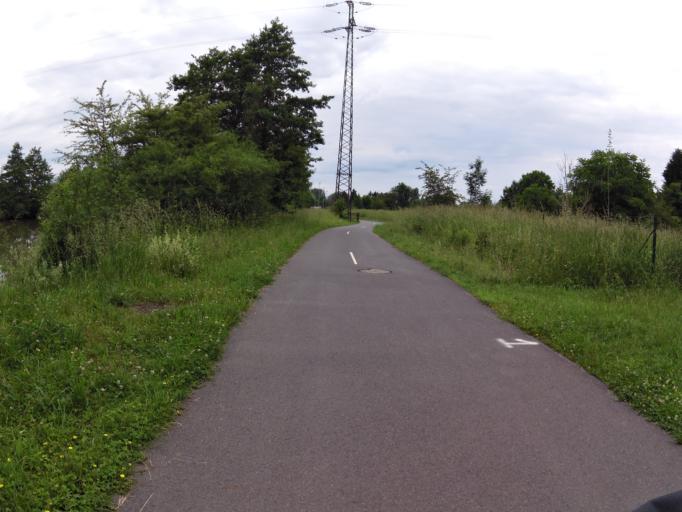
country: FR
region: Champagne-Ardenne
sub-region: Departement des Ardennes
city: Villers-Semeuse
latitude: 49.7565
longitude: 4.7443
